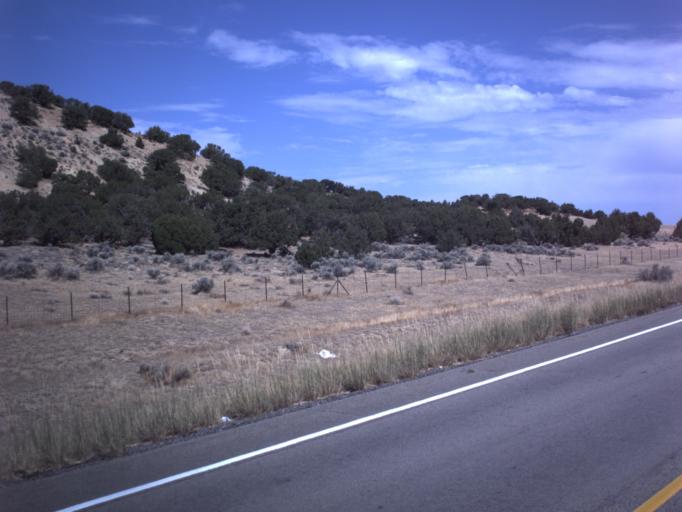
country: US
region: Utah
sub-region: Sanpete County
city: Gunnison
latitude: 39.3859
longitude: -111.9278
